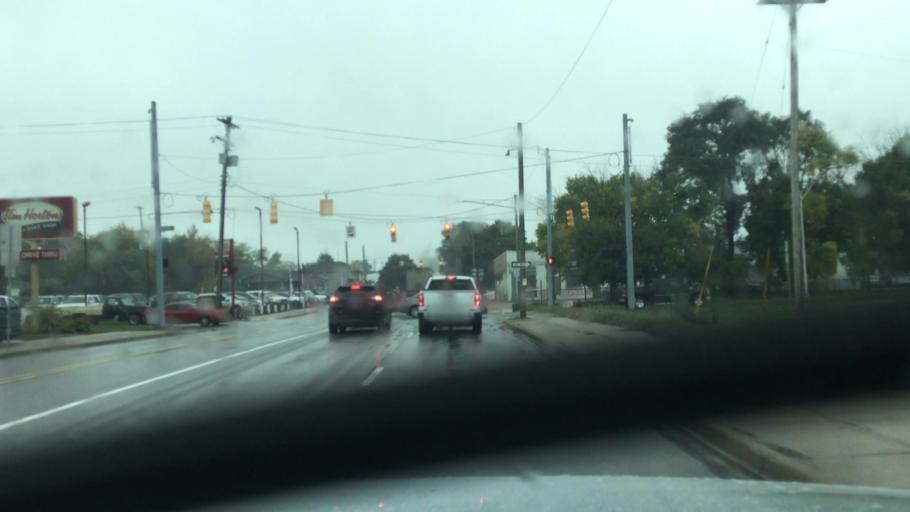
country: US
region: Michigan
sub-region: Saginaw County
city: Saginaw
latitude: 43.4360
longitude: -83.9488
